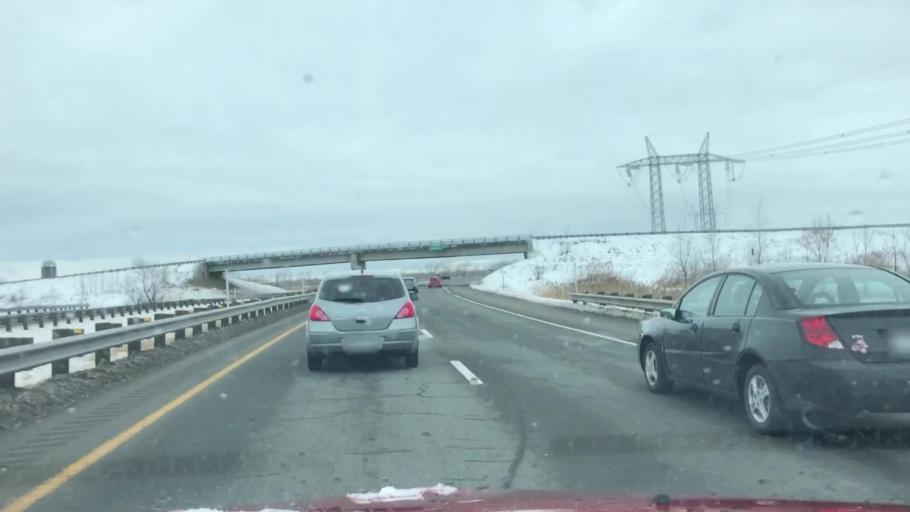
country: CA
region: Quebec
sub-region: Monteregie
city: Saint-Cesaire
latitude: 45.3718
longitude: -73.0378
